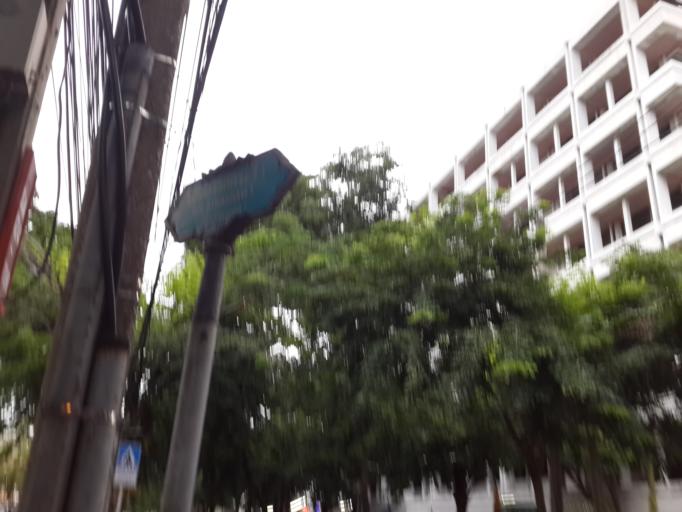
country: TH
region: Bangkok
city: Khlong Toei
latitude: 13.7217
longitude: 100.5690
